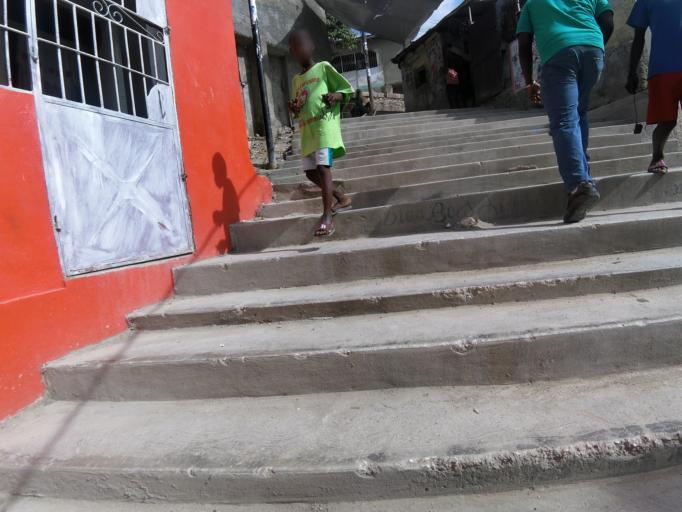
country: HT
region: Ouest
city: Port-au-Prince
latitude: 18.5248
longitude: -72.3344
